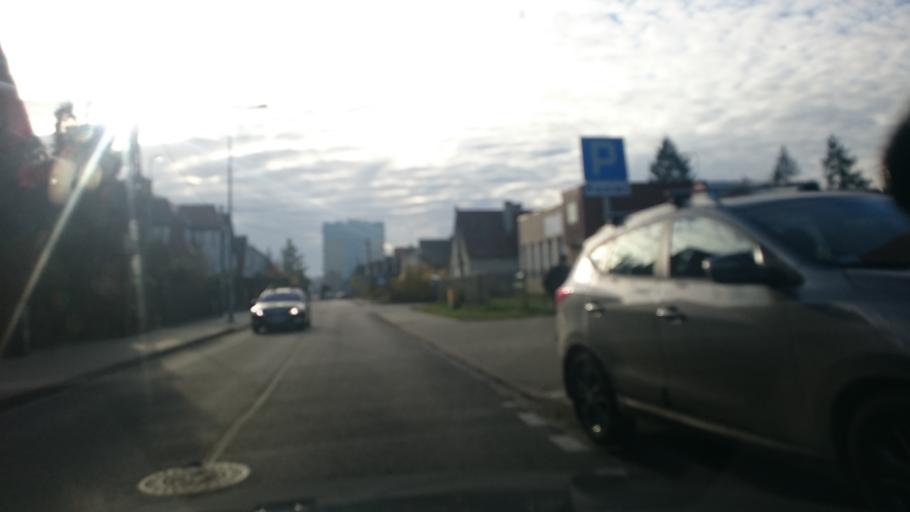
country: PL
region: Pomeranian Voivodeship
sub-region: Sopot
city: Sopot
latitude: 54.4049
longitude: 18.5778
